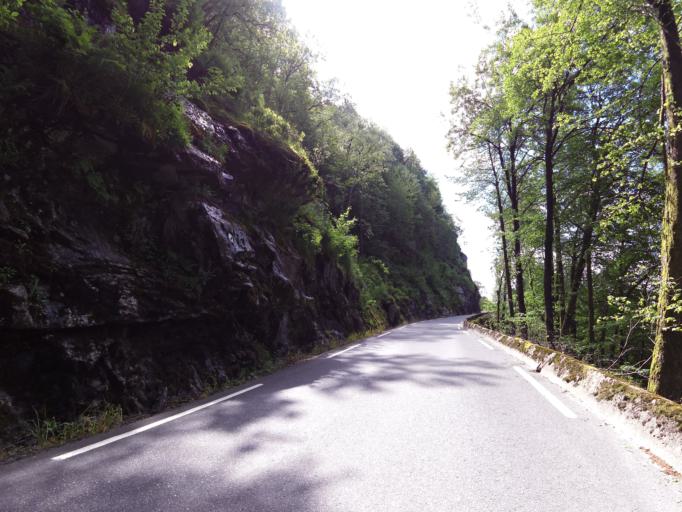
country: NO
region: Vest-Agder
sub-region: Kvinesdal
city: Liknes
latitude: 58.2949
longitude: 6.9454
